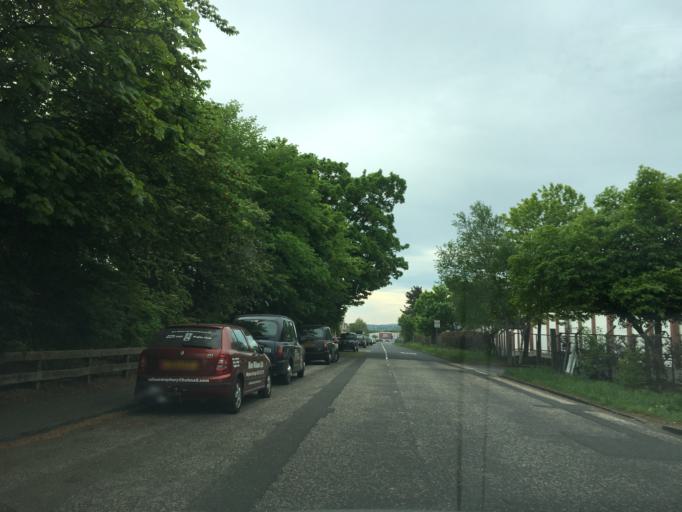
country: GB
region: Scotland
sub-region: Edinburgh
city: Currie
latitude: 55.9429
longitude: -3.3194
